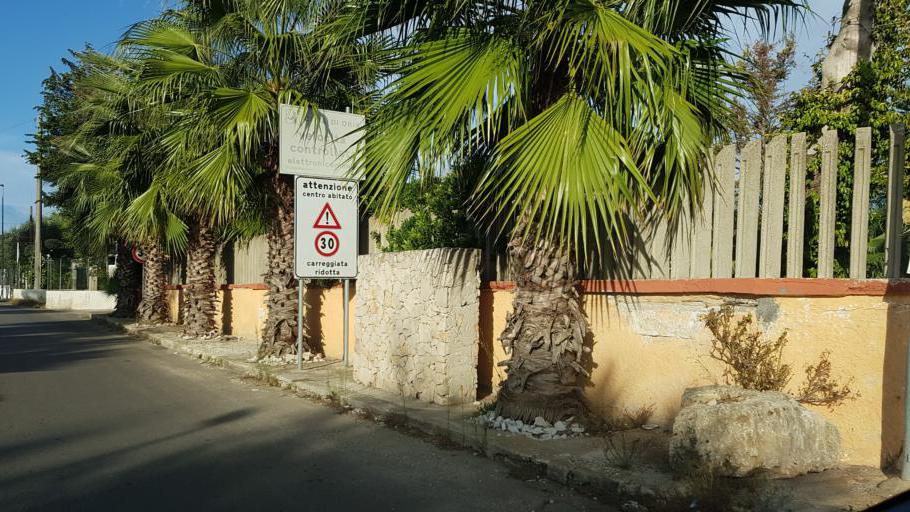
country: IT
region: Apulia
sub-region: Provincia di Brindisi
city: Oria
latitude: 40.5090
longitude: 17.6497
